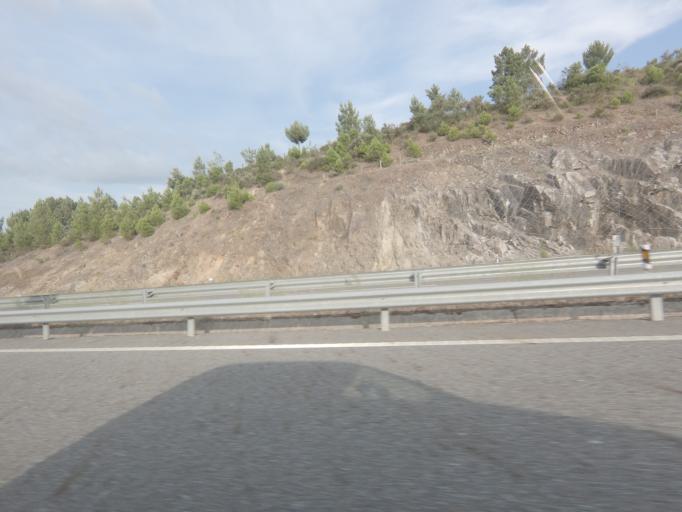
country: PT
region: Vila Real
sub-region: Boticas
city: Boticas
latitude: 41.6608
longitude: -7.5773
